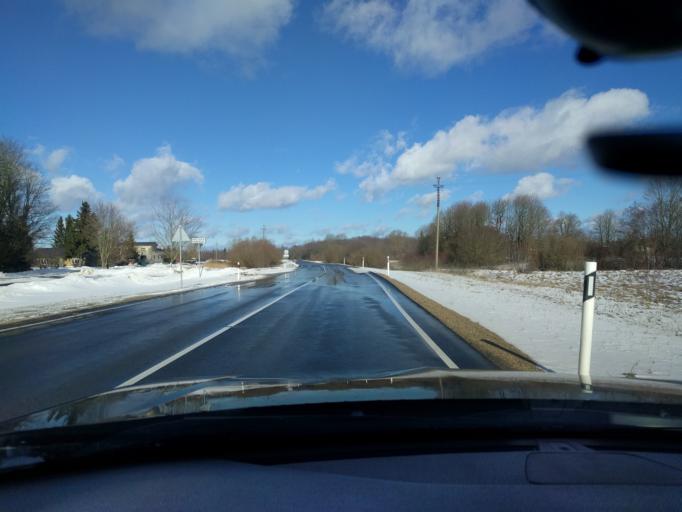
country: EE
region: Harju
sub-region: Raasiku vald
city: Raasiku
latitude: 59.2994
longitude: 25.1732
